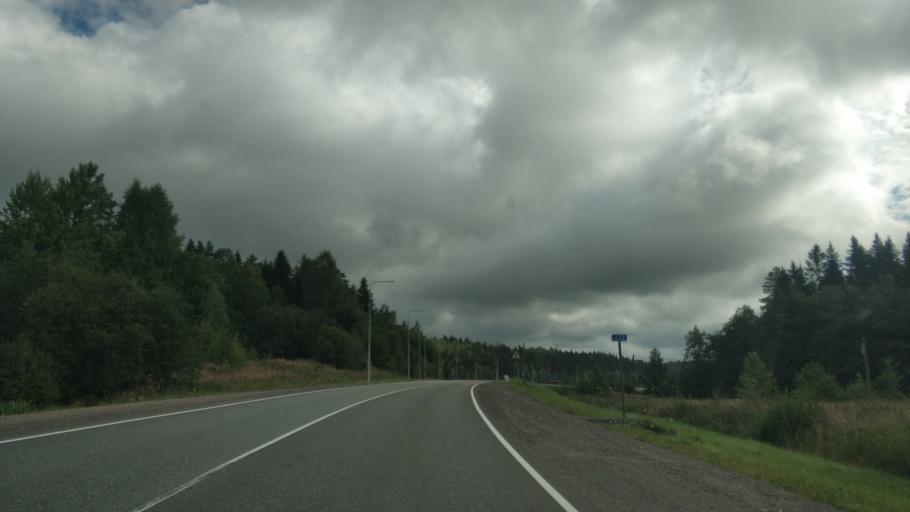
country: RU
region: Republic of Karelia
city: Khelyulya
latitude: 61.7738
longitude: 30.6568
